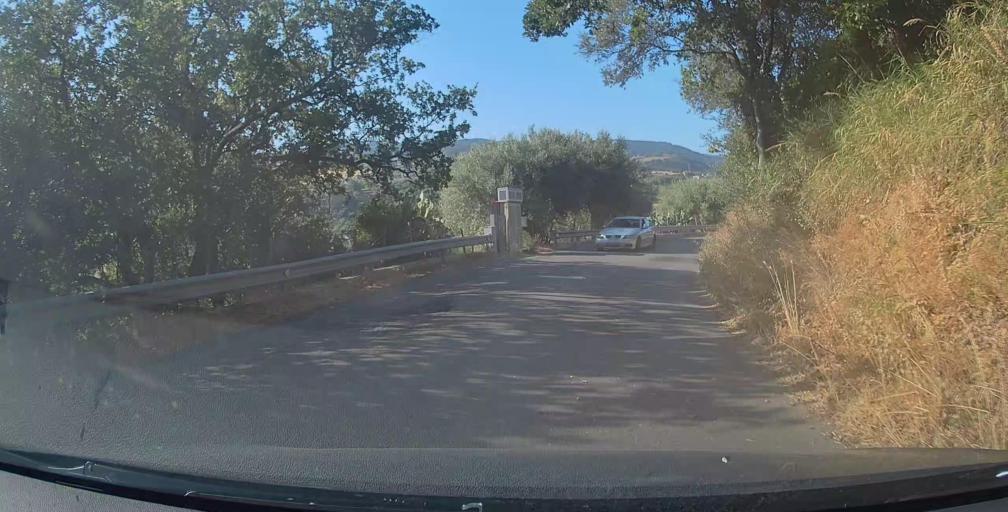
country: IT
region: Sicily
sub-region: Messina
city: Librizzi
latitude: 38.0812
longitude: 14.9747
